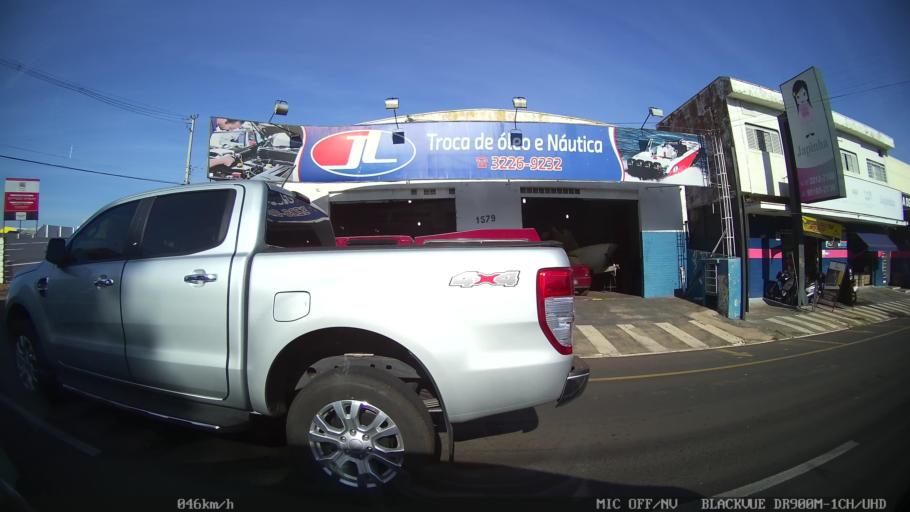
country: BR
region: Sao Paulo
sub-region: Sao Jose Do Rio Preto
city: Sao Jose do Rio Preto
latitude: -20.7961
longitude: -49.3645
